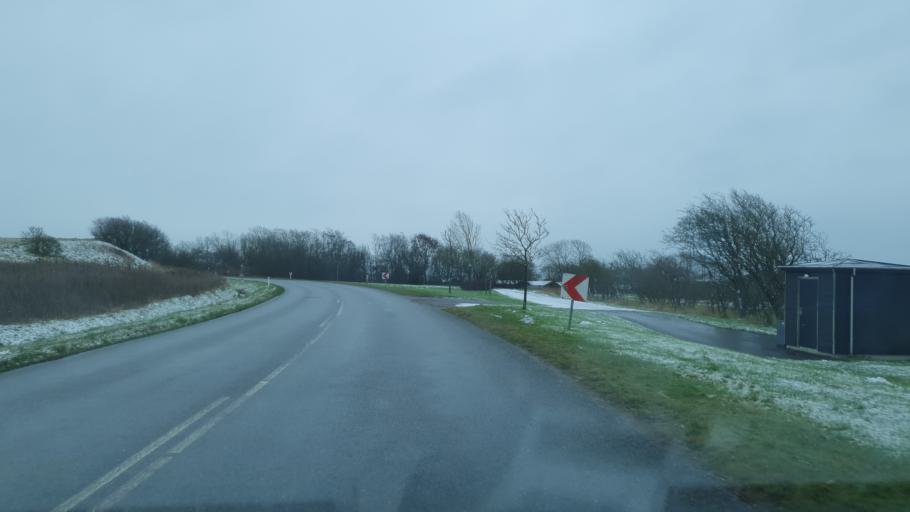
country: DK
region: North Denmark
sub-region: Jammerbugt Kommune
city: Brovst
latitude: 57.1033
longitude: 9.5030
